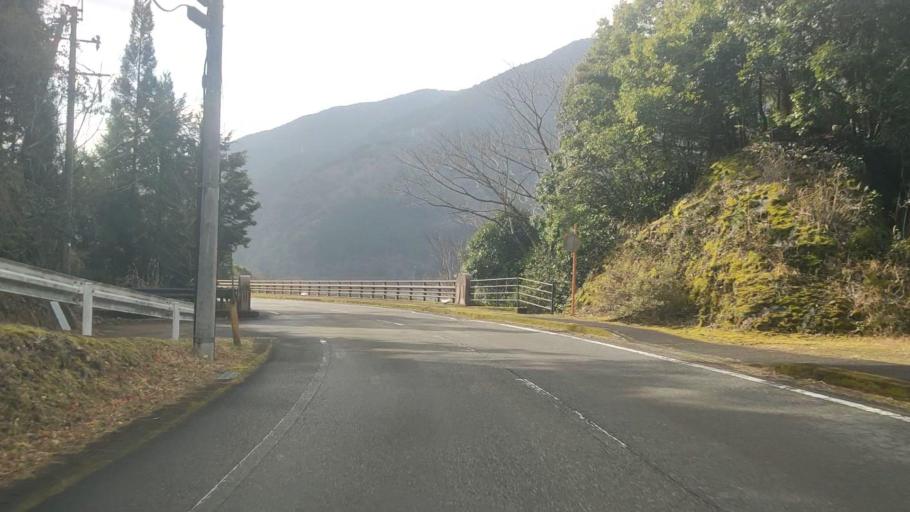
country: JP
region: Kumamoto
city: Hitoyoshi
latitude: 32.4039
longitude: 130.8257
